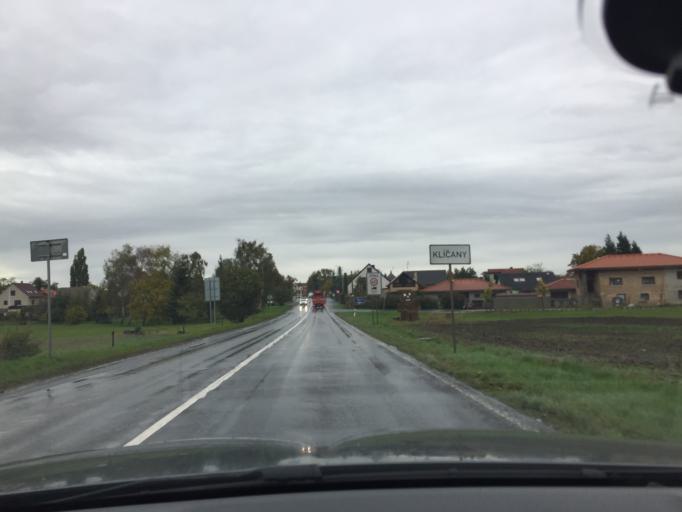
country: CZ
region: Central Bohemia
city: Klecany
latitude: 50.1982
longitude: 14.4359
